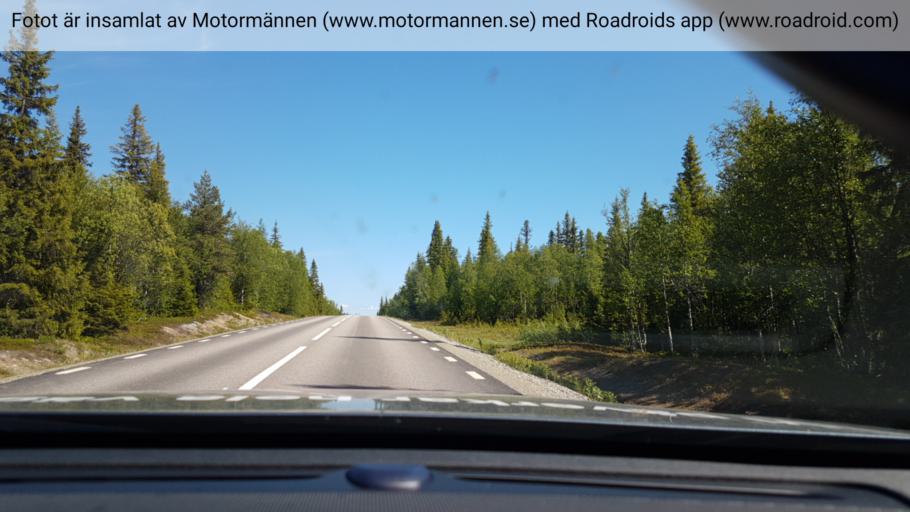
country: SE
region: Vaesterbotten
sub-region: Asele Kommun
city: Insjon
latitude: 64.7294
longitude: 17.4784
